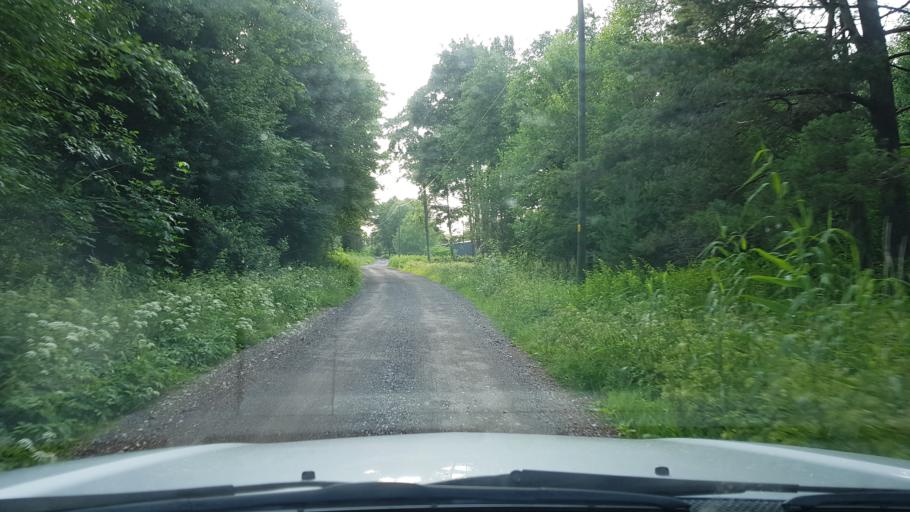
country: EE
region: Ida-Virumaa
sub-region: Narva-Joesuu linn
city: Narva-Joesuu
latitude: 59.4569
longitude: 28.0683
